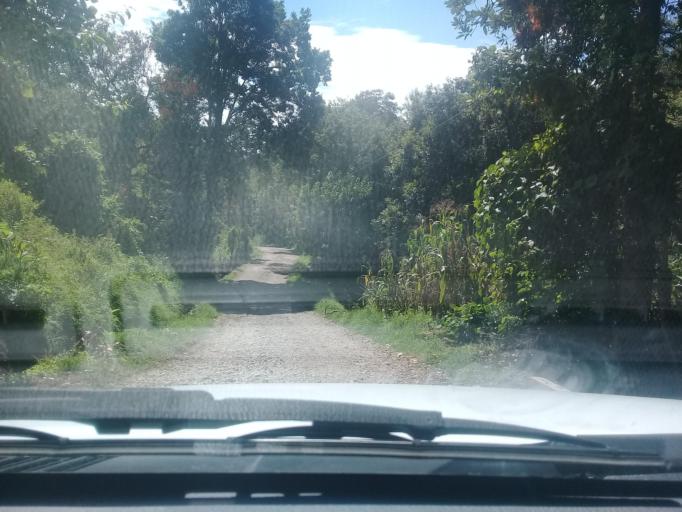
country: MX
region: Veracruz
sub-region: Tlalnelhuayocan
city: Otilpan
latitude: 19.5679
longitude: -96.9871
